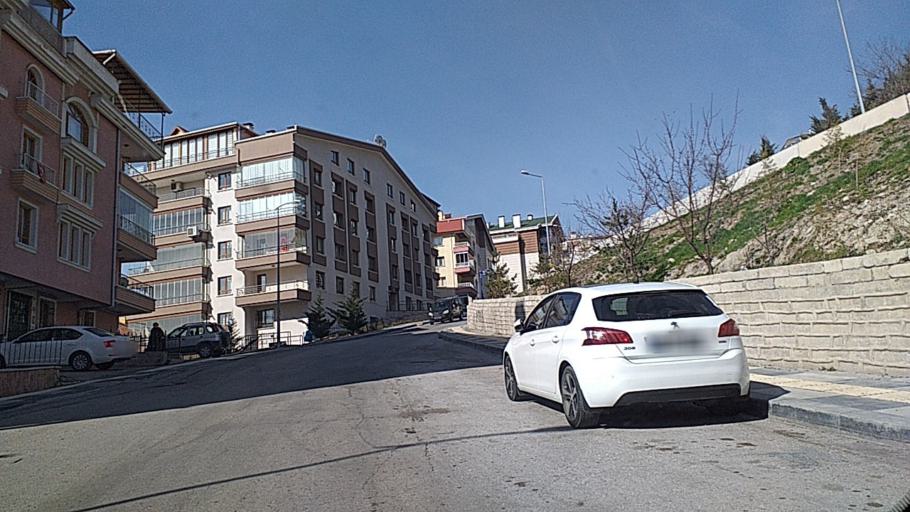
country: TR
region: Ankara
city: Ankara
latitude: 39.9891
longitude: 32.8173
